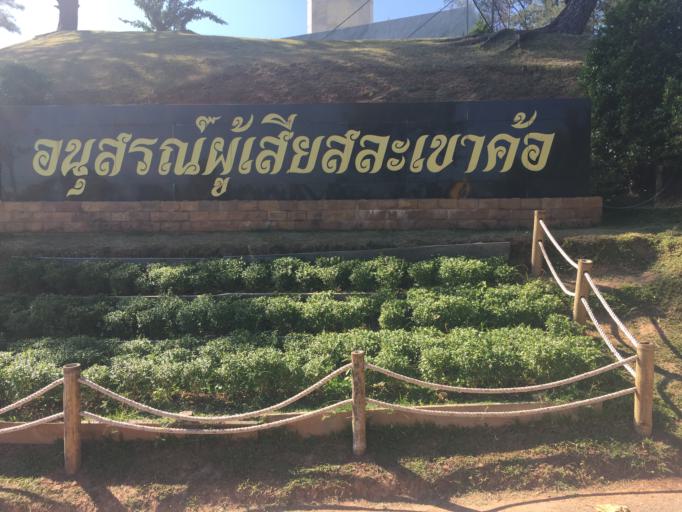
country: TH
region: Phetchabun
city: Khao Kho
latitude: 16.6149
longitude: 100.9858
